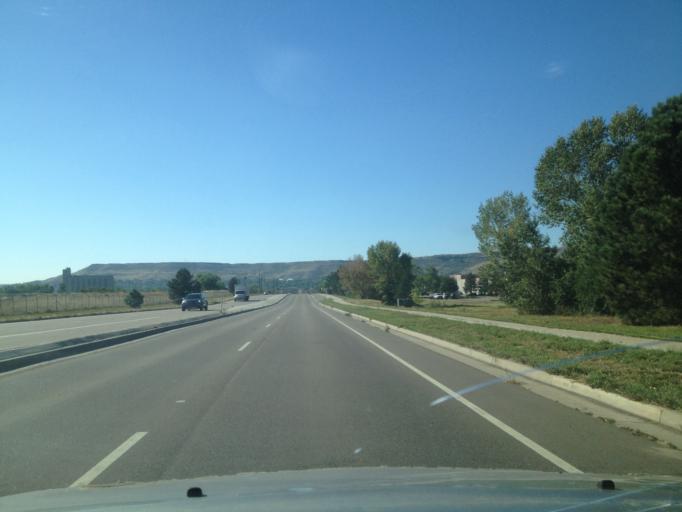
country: US
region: Colorado
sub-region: Jefferson County
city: Applewood
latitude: 39.7820
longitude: -105.1749
